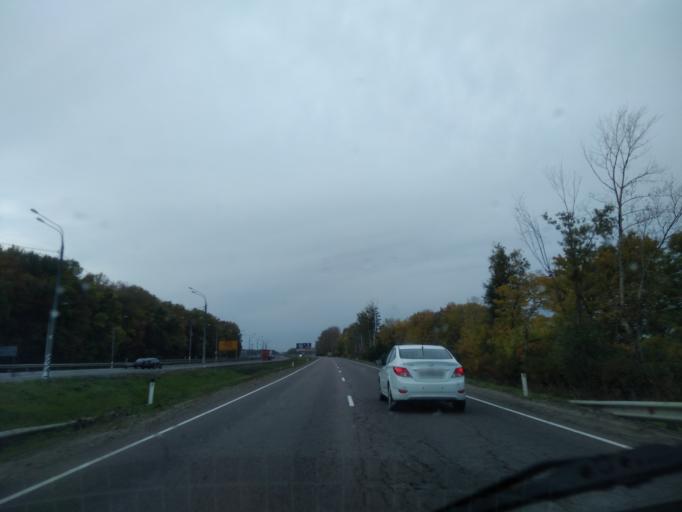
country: RU
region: Lipetsk
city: Zadonsk
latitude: 52.4402
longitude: 38.8055
